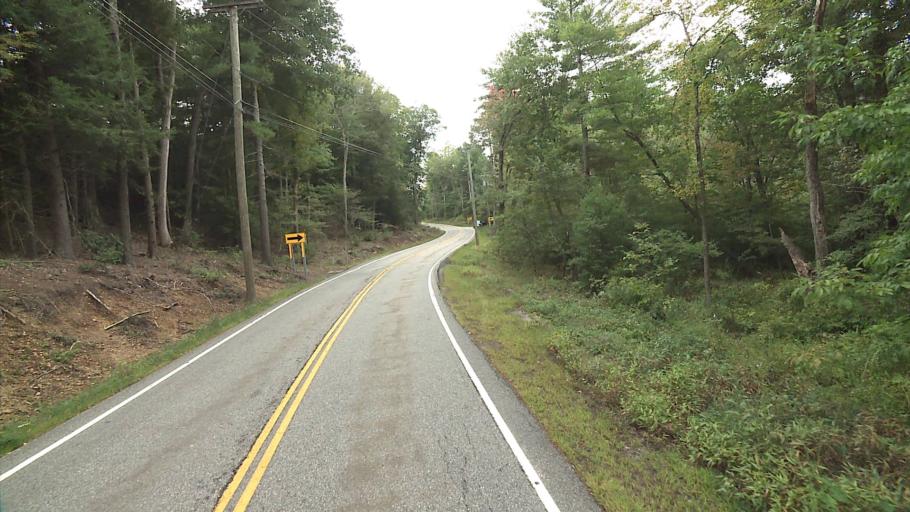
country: US
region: Connecticut
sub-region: Tolland County
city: Stafford Springs
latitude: 41.9142
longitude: -72.2618
